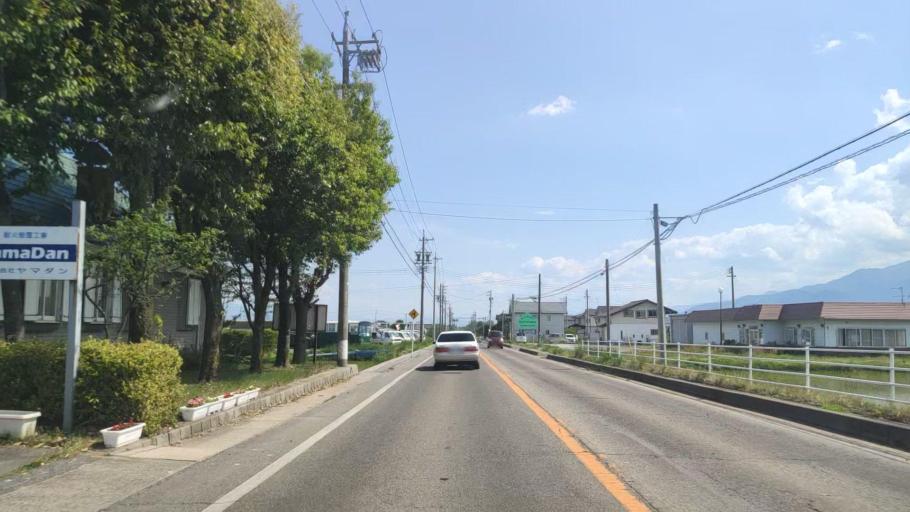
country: JP
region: Nagano
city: Hotaka
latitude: 36.3916
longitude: 137.8640
